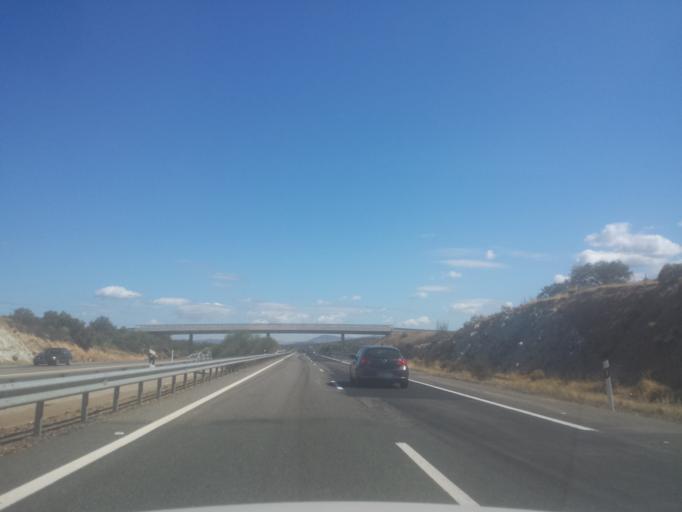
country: ES
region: Andalusia
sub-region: Provincia de Huelva
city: Santa Olalla del Cala
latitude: 37.8415
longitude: -6.2200
